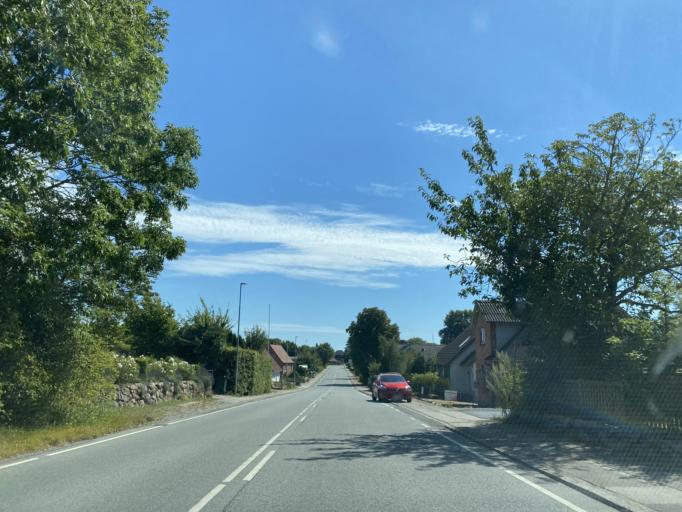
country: DK
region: South Denmark
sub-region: Faaborg-Midtfyn Kommune
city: Ringe
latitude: 55.2386
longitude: 10.5597
